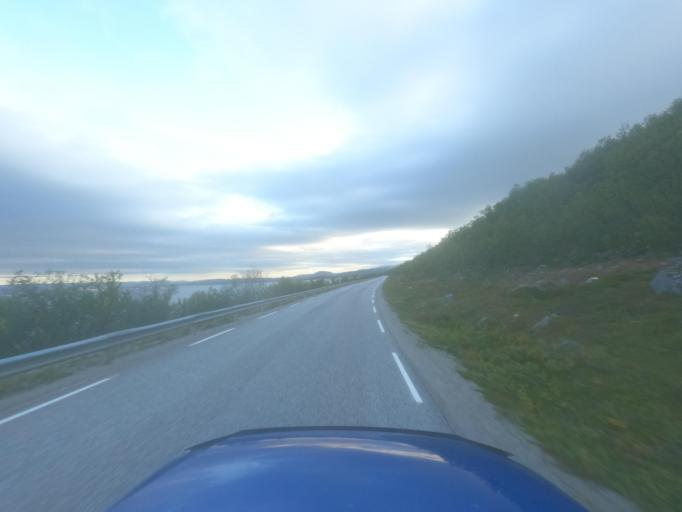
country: NO
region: Finnmark Fylke
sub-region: Porsanger
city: Lakselv
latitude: 70.3998
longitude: 25.1345
